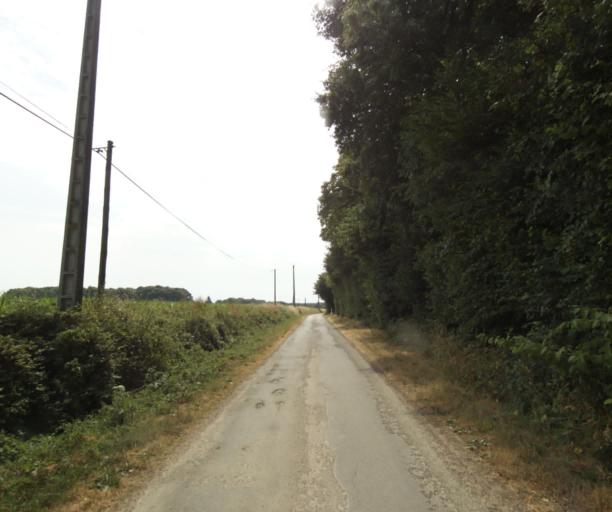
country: FR
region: Centre
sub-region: Departement d'Eure-et-Loir
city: Authon-du-Perche
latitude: 48.1882
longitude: 0.9423
